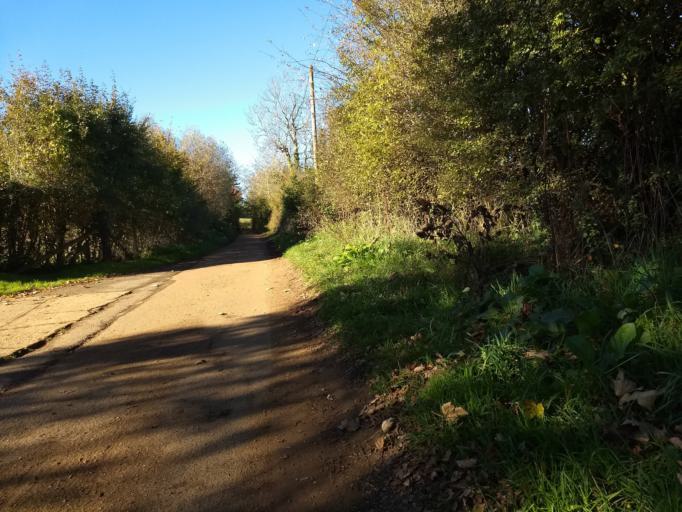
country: GB
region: England
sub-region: Isle of Wight
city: Newport
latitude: 50.6670
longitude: -1.2782
